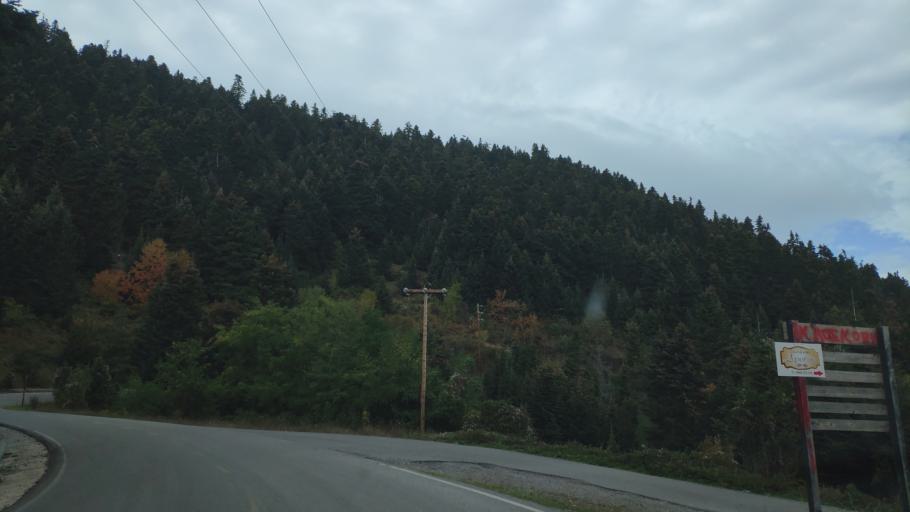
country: GR
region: Central Greece
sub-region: Nomos Fokidos
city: Amfissa
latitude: 38.6953
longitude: 22.3182
